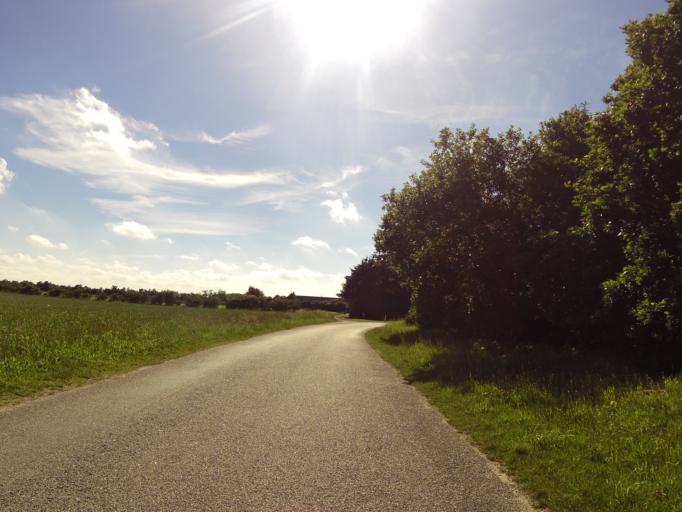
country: DK
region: South Denmark
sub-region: Aabenraa Kommune
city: Rodekro
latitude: 55.0779
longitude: 9.1968
